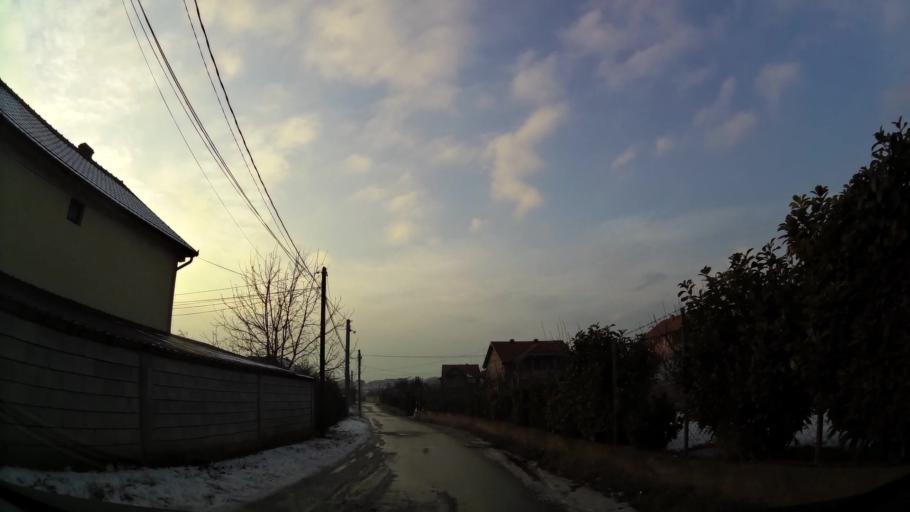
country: MK
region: Aracinovo
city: Arachinovo
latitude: 42.0272
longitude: 21.5557
